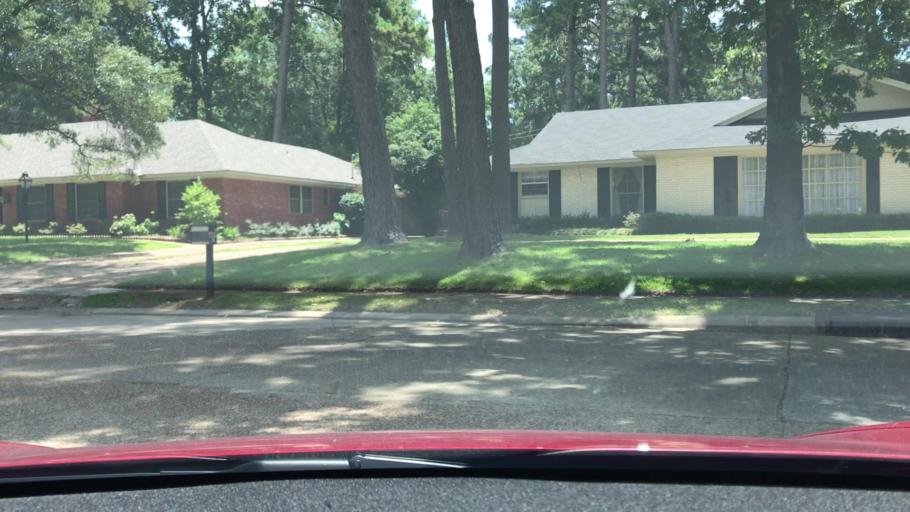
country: US
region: Louisiana
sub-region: Bossier Parish
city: Bossier City
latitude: 32.4281
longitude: -93.7358
